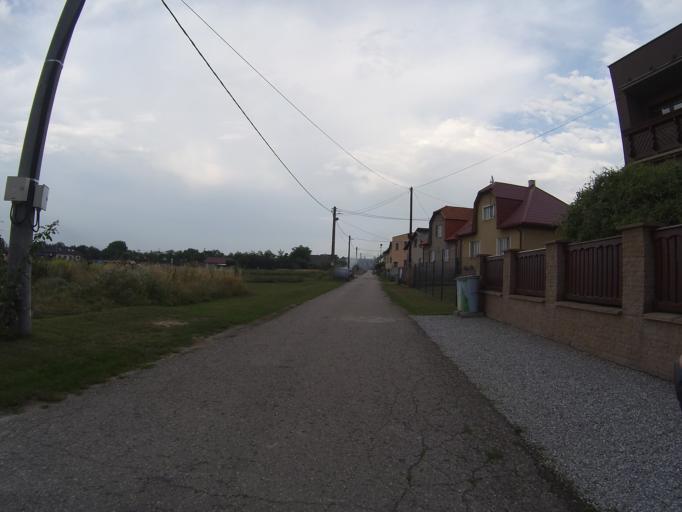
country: SK
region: Nitriansky
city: Ilava
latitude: 49.0366
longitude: 18.3095
